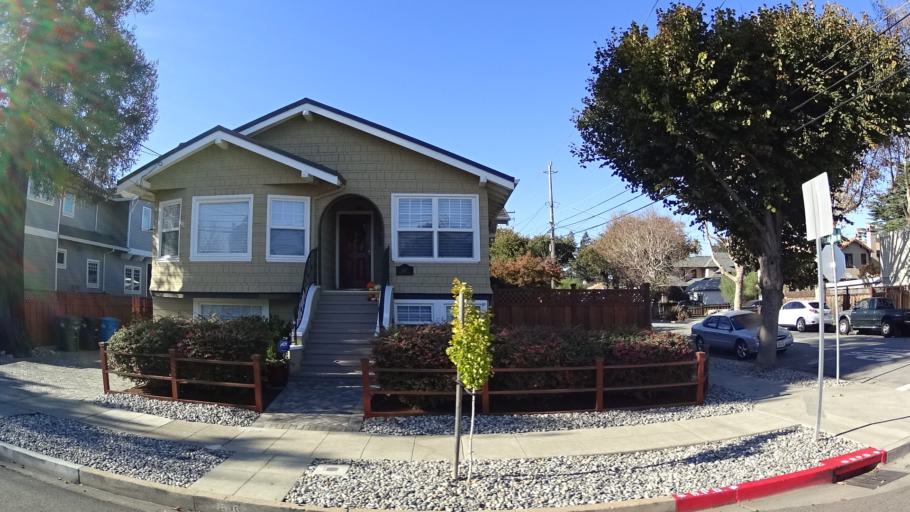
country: US
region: California
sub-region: San Mateo County
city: San Mateo
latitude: 37.5810
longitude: -122.3372
